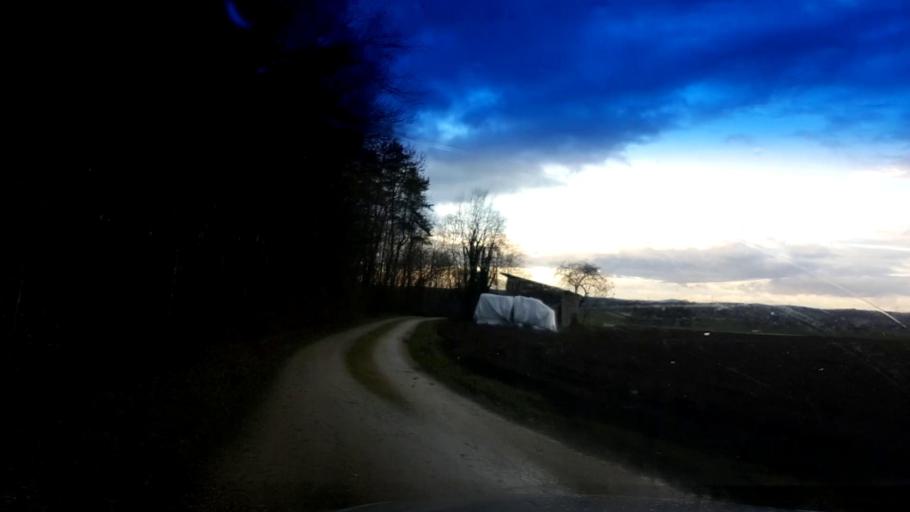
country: DE
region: Bavaria
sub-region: Upper Franconia
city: Schesslitz
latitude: 49.9490
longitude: 11.0245
